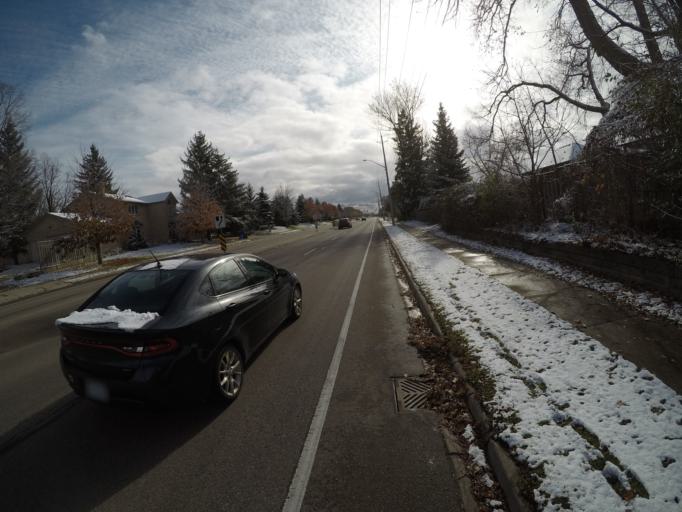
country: CA
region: Ontario
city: Waterloo
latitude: 43.5018
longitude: -80.4948
